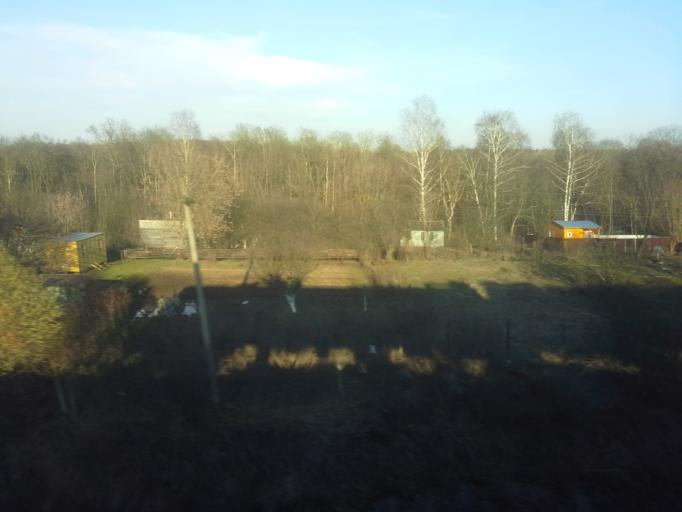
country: RU
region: Moskovskaya
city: Podosinki
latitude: 56.1970
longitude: 37.5246
